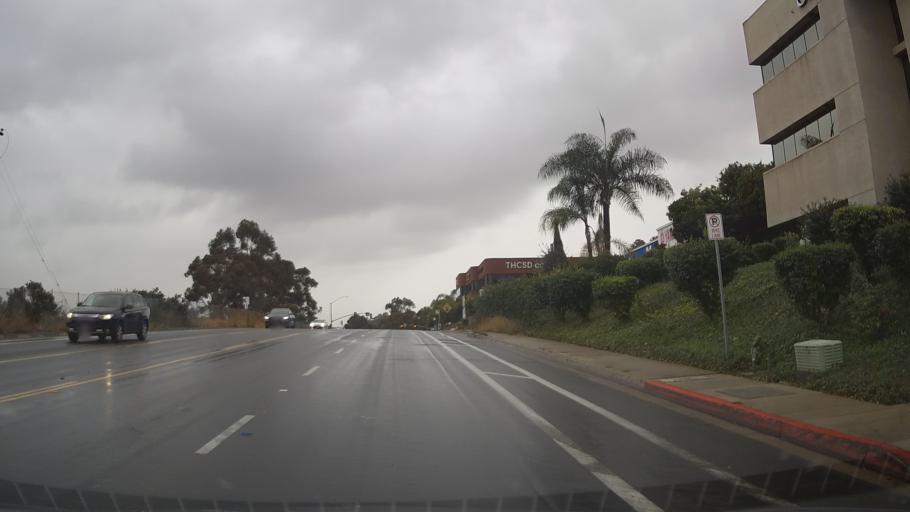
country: US
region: California
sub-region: San Diego County
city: San Diego
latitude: 32.7779
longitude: -117.1168
